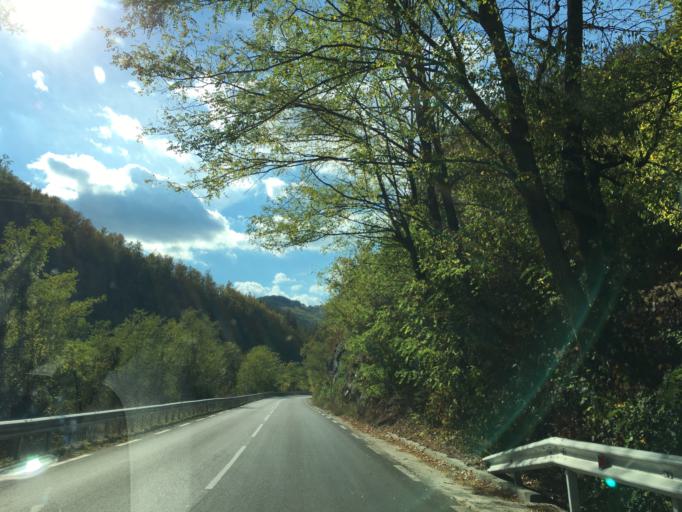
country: BG
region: Smolyan
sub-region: Obshtina Zlatograd
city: Zlatograd
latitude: 41.3950
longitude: 25.0773
